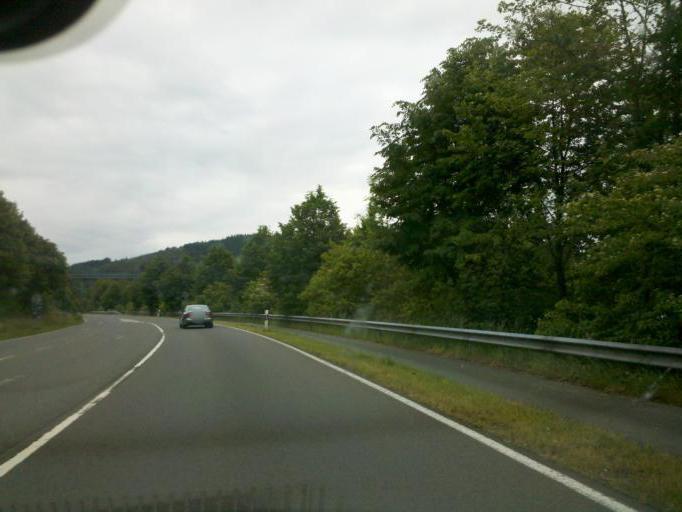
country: DE
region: North Rhine-Westphalia
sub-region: Regierungsbezirk Arnsberg
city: Olpe
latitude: 51.0404
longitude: 7.8632
